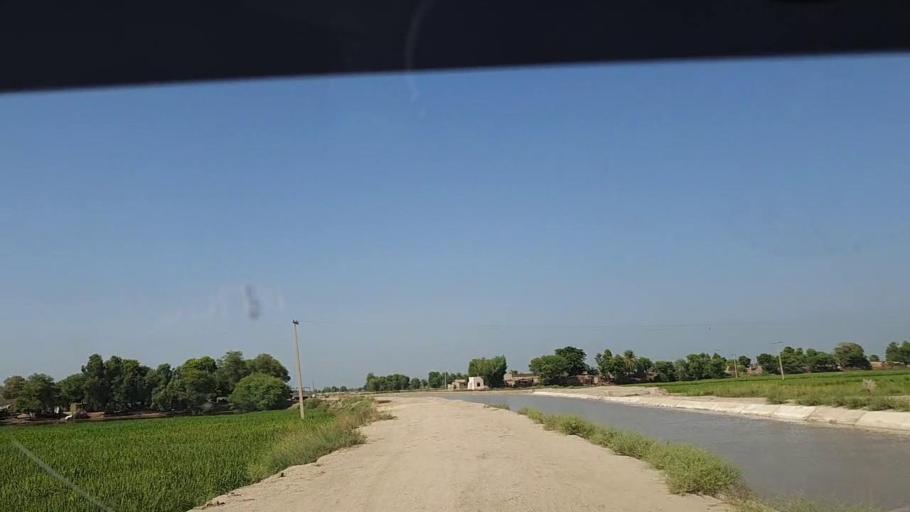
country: PK
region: Sindh
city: Ghauspur
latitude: 28.1733
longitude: 69.0990
